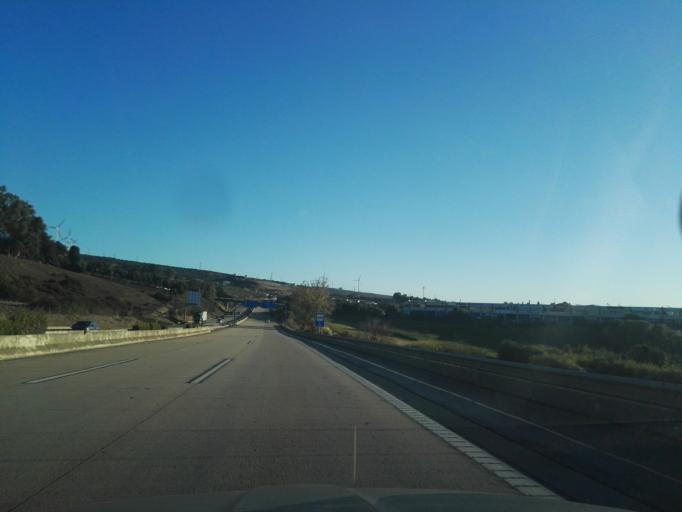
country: PT
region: Lisbon
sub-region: Loures
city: Santo Antao do Tojal
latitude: 38.8614
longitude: -9.1558
